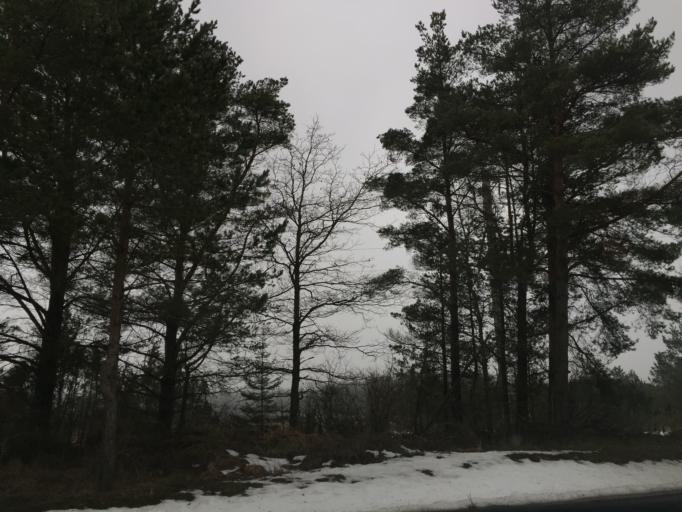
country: EE
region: Saare
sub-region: Orissaare vald
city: Orissaare
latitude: 58.4163
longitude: 22.8243
